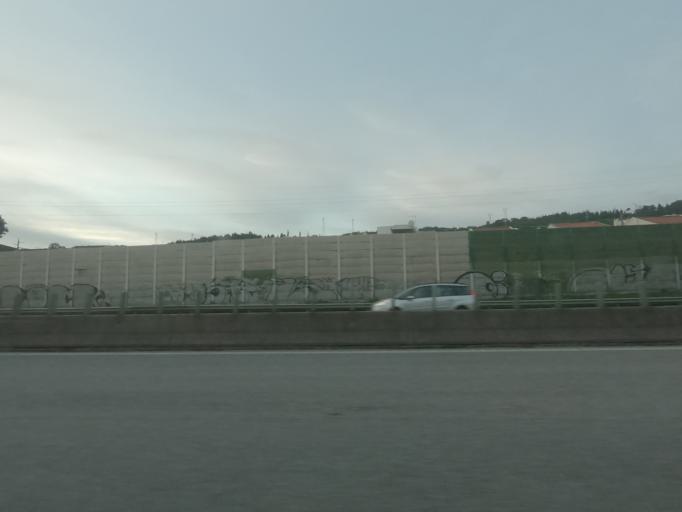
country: PT
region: Lisbon
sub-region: Vila Franca de Xira
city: Sobralinho
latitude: 38.9179
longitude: -9.0208
